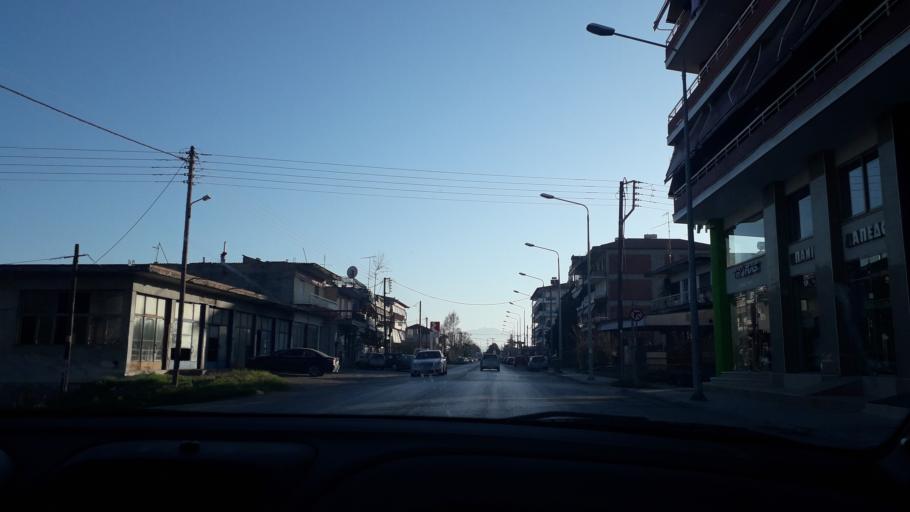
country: GR
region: Central Macedonia
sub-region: Nomos Imathias
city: Alexandreia
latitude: 40.6239
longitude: 22.4477
